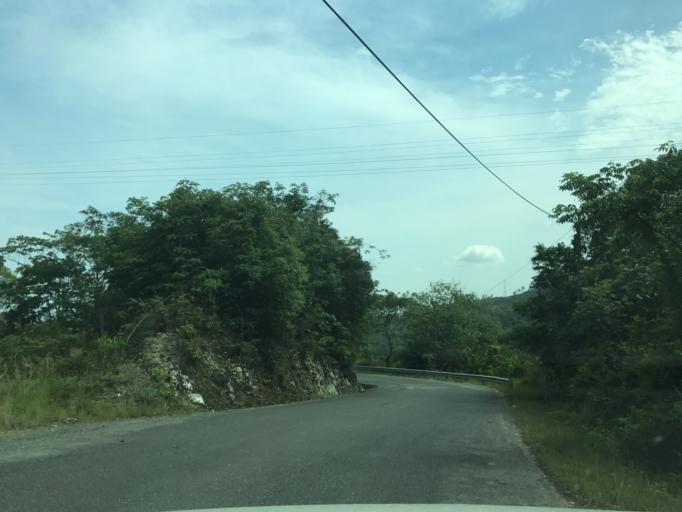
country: GT
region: Izabal
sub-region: Municipio de Los Amates
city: Los Amates
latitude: 15.3849
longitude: -89.0217
